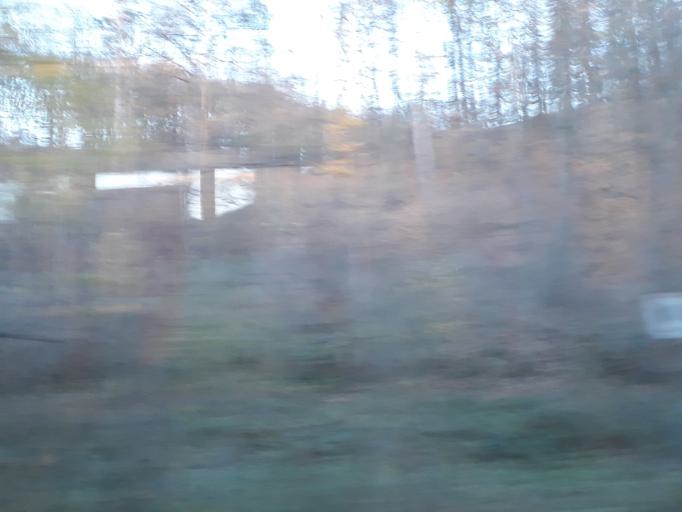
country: DE
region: Saxony
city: Reinhardtsgrimma
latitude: 50.9145
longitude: 13.7867
